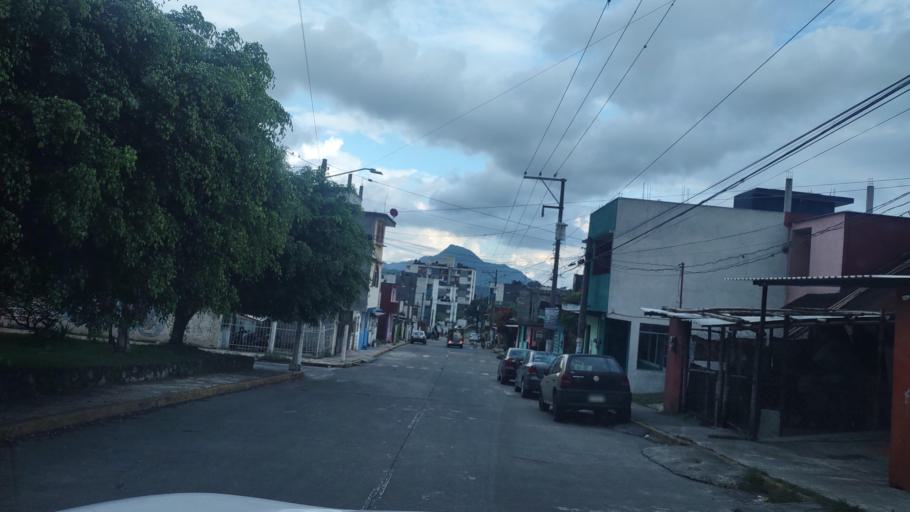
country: MX
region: Veracruz
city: Ixtac Zoquitlan
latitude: 18.8834
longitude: -97.0638
